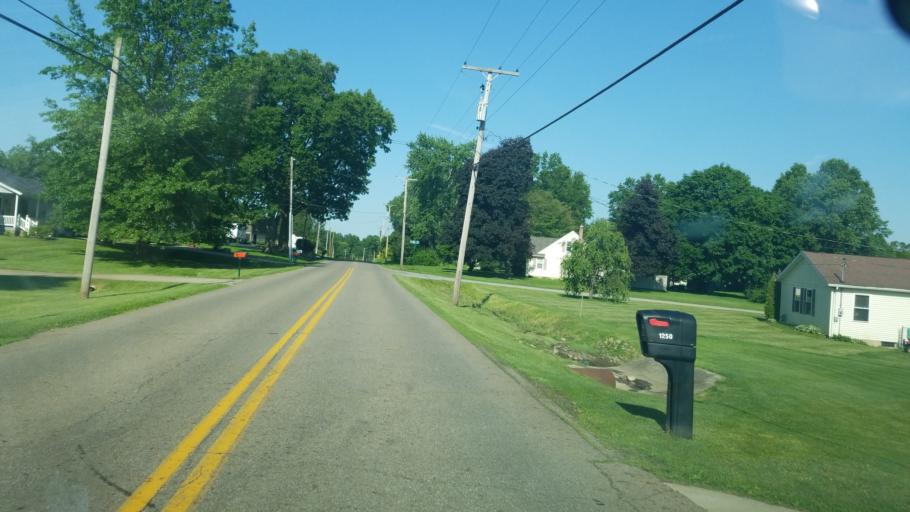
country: US
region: Ohio
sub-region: Wayne County
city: Wooster
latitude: 40.7804
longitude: -81.9648
